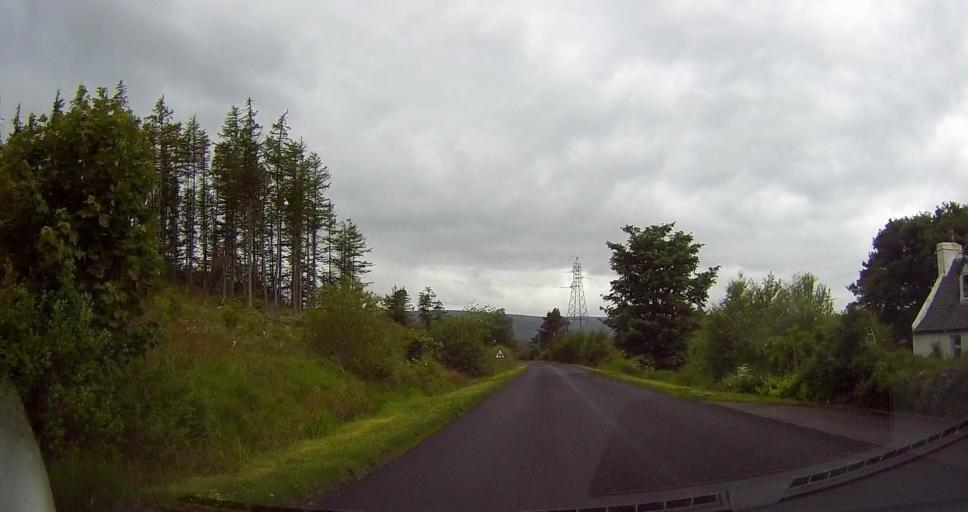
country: GB
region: Scotland
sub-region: Highland
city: Alness
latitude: 58.0242
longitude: -4.3826
